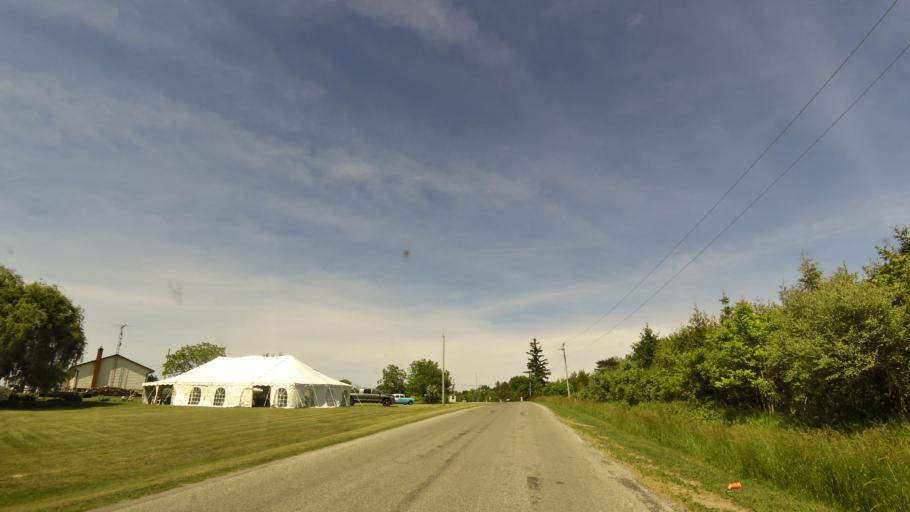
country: CA
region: Ontario
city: Norfolk County
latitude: 42.7525
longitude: -80.2682
